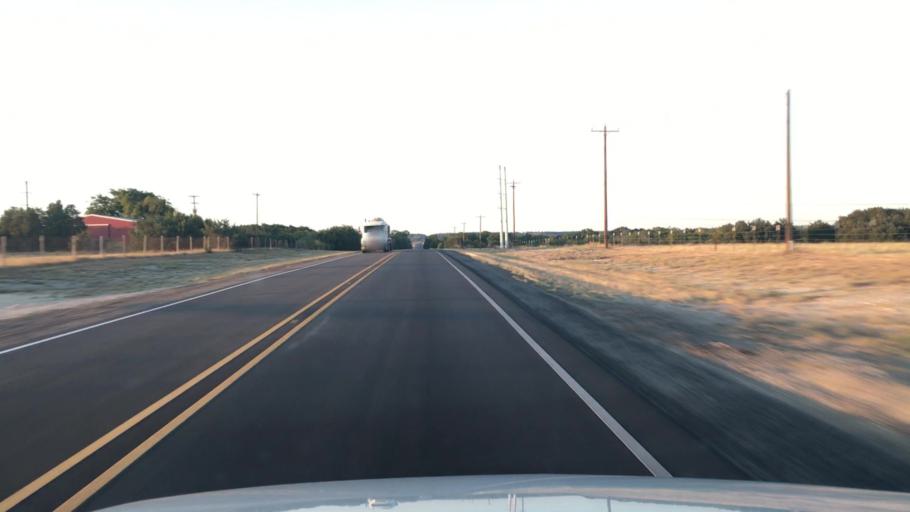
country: US
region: Texas
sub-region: Hamilton County
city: Hico
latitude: 32.0614
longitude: -97.9949
